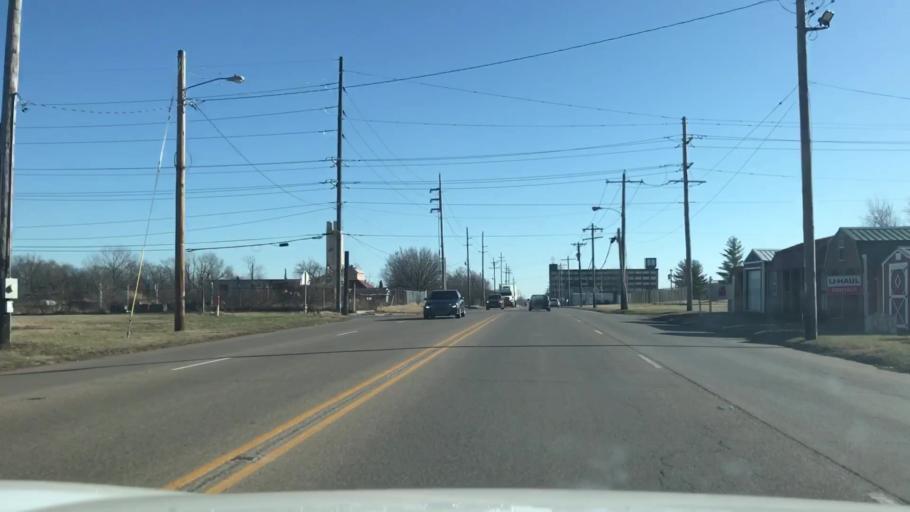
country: US
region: Illinois
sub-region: Saint Clair County
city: Alorton
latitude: 38.6038
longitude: -90.1325
